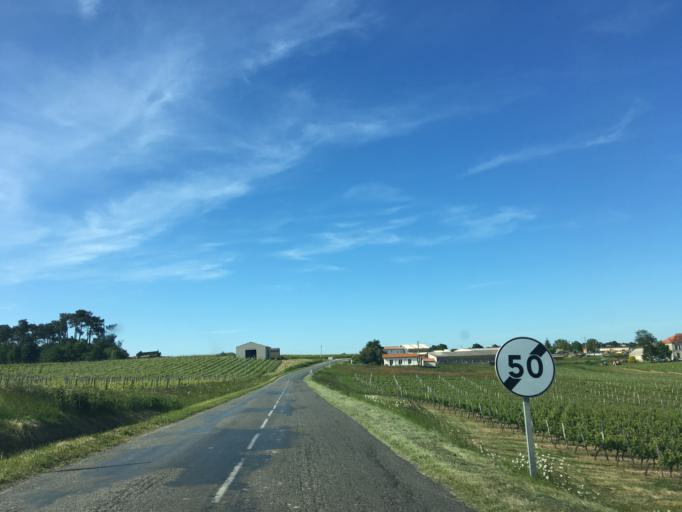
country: FR
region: Aquitaine
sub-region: Departement de la Gironde
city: Saint-Ciers-sur-Gironde
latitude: 45.3323
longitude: -0.5941
